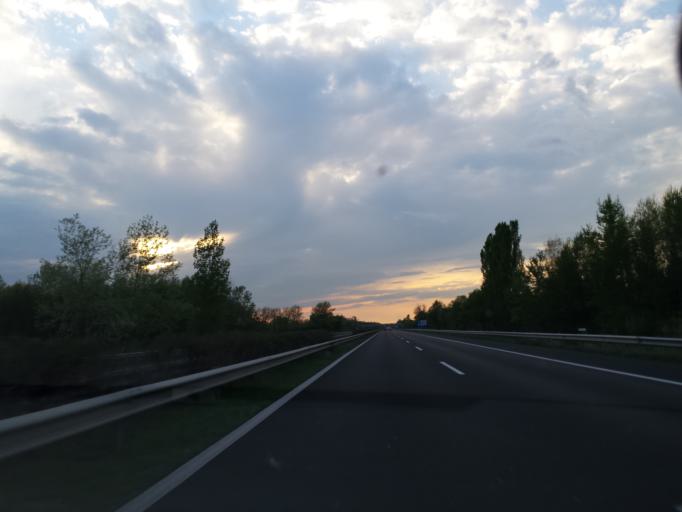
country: HU
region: Gyor-Moson-Sopron
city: Kimle
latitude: 47.7840
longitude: 17.3418
